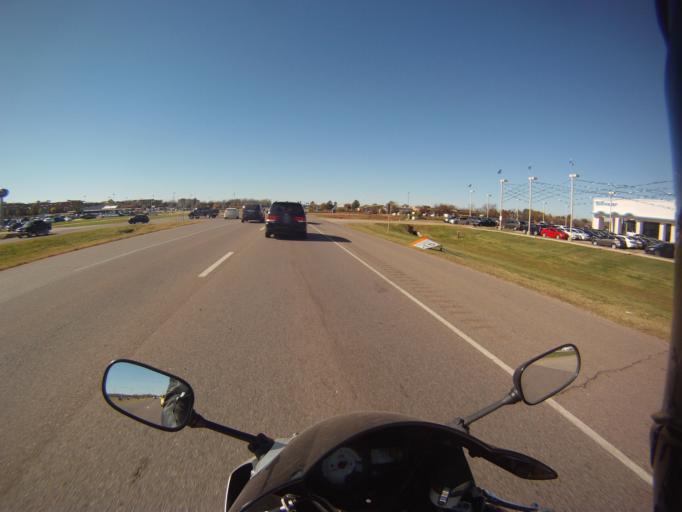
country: US
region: Oklahoma
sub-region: Payne County
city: Stillwater
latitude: 36.1158
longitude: -97.1156
